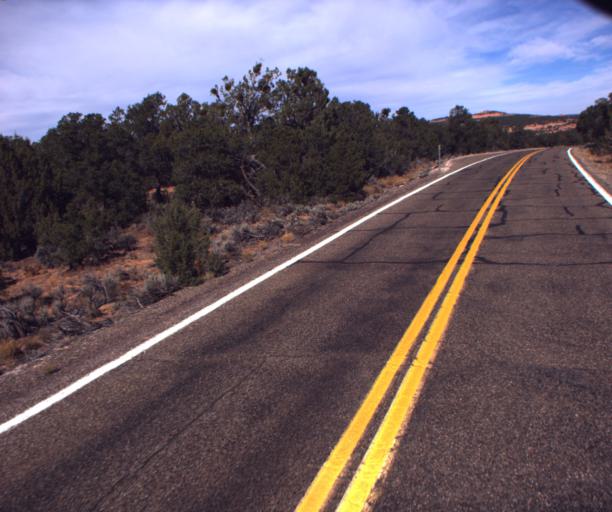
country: US
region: Arizona
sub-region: Navajo County
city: Kayenta
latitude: 36.6476
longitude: -110.5180
